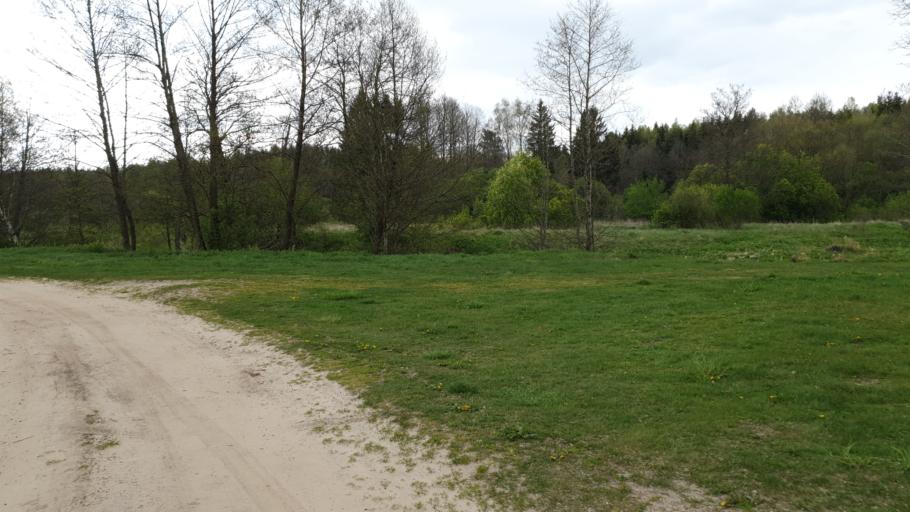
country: BY
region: Minsk
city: Rakaw
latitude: 53.9807
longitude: 26.9710
